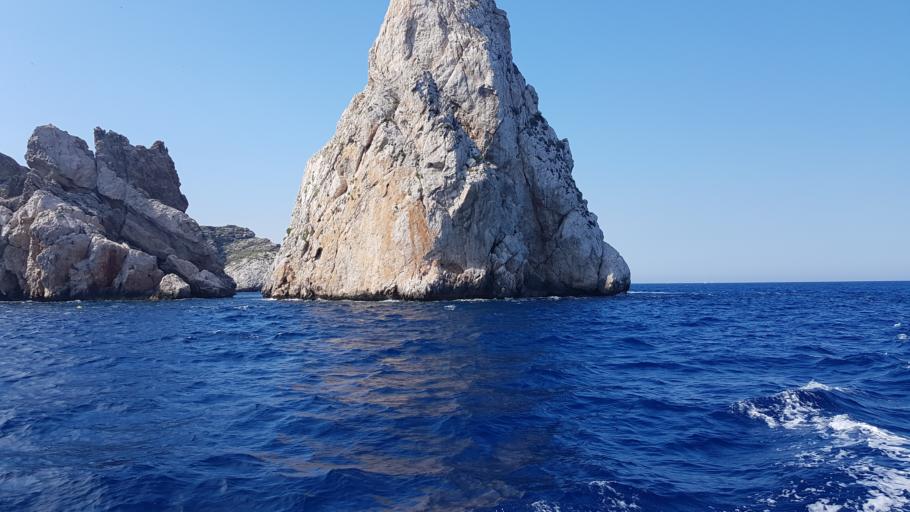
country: ES
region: Catalonia
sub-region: Provincia de Girona
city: Begur
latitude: 42.0405
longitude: 3.2284
